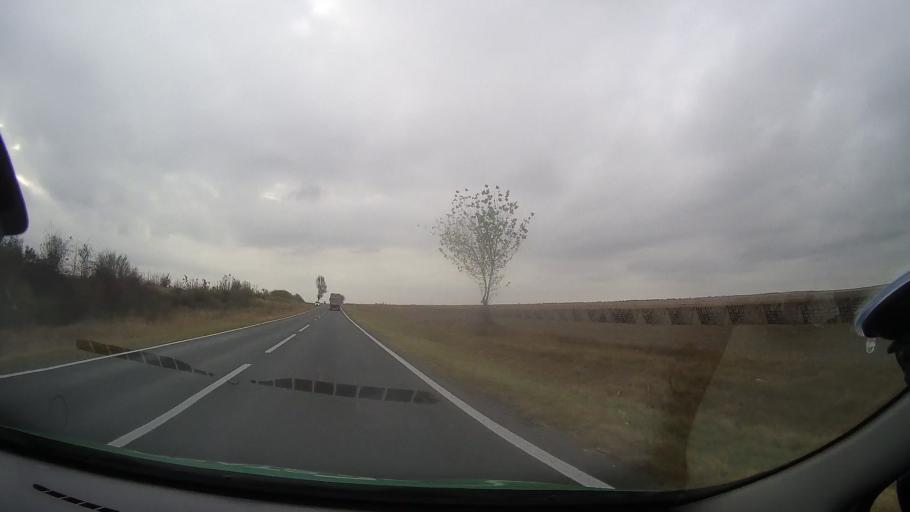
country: RO
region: Constanta
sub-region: Comuna Castelu
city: Castelu
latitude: 44.2534
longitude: 28.3205
